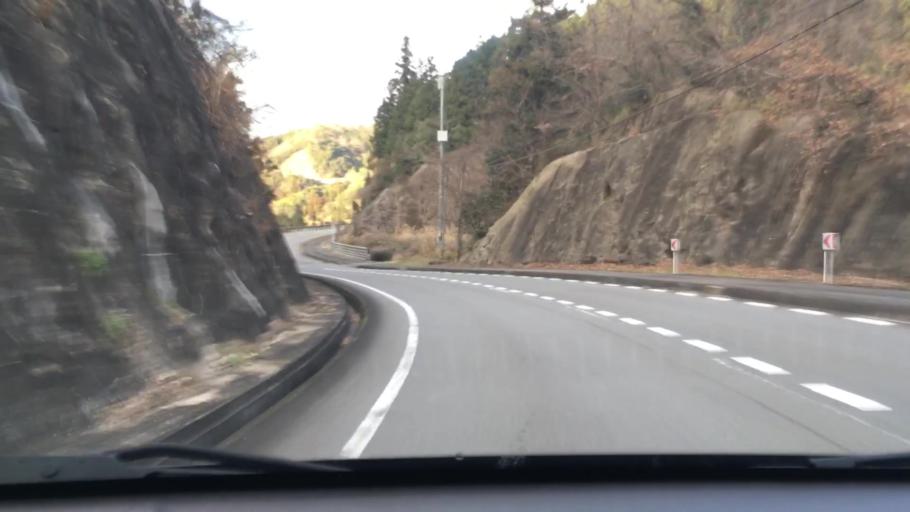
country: JP
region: Oita
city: Hiji
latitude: 33.4254
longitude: 131.4140
